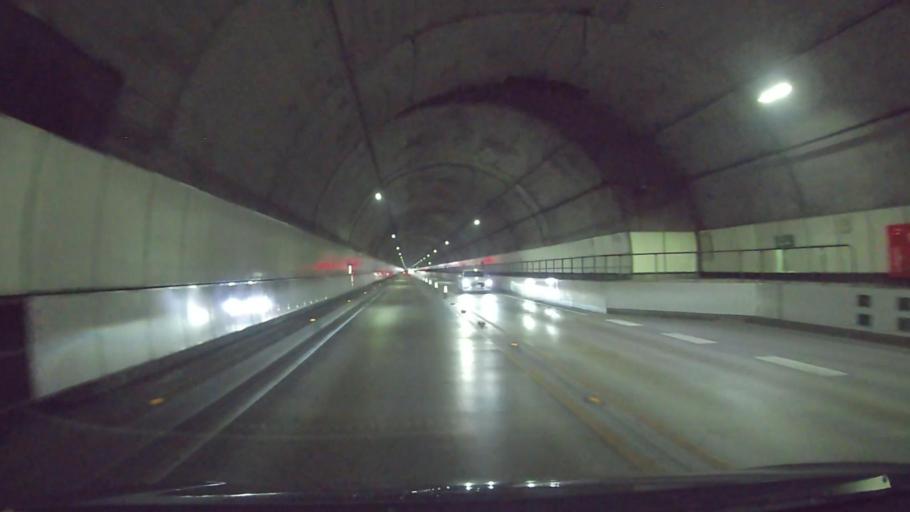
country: JP
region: Saitama
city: Yorii
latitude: 36.0911
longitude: 139.1404
